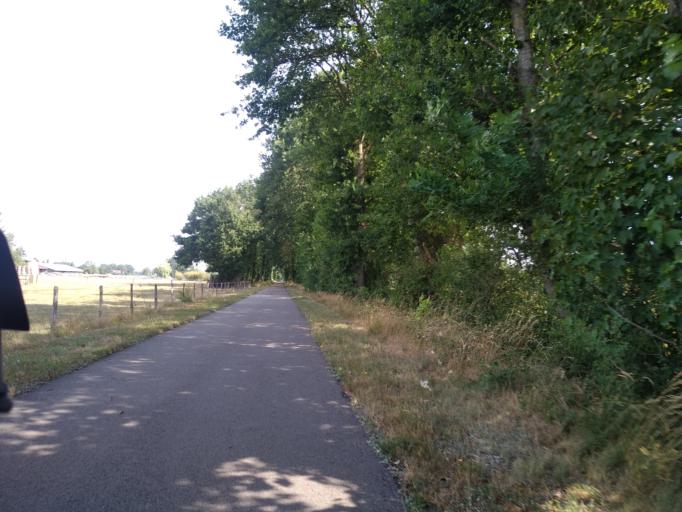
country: FR
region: Bourgogne
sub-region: Departement de Saone-et-Loire
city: Marcigny
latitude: 46.3412
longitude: 4.0283
